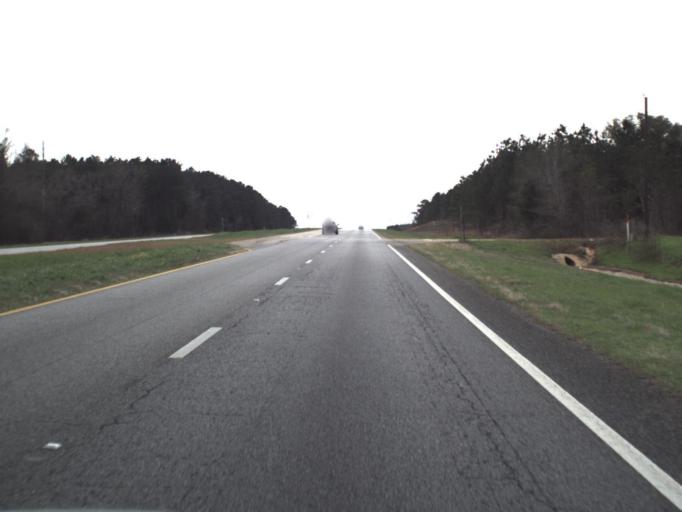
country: US
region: Florida
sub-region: Jackson County
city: Marianna
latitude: 30.8366
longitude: -85.3509
